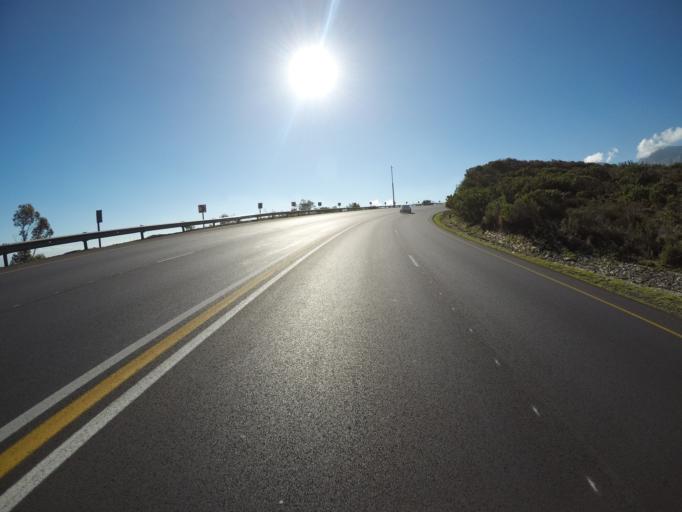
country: ZA
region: Western Cape
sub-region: Overberg District Municipality
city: Grabouw
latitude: -34.1289
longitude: 18.9302
